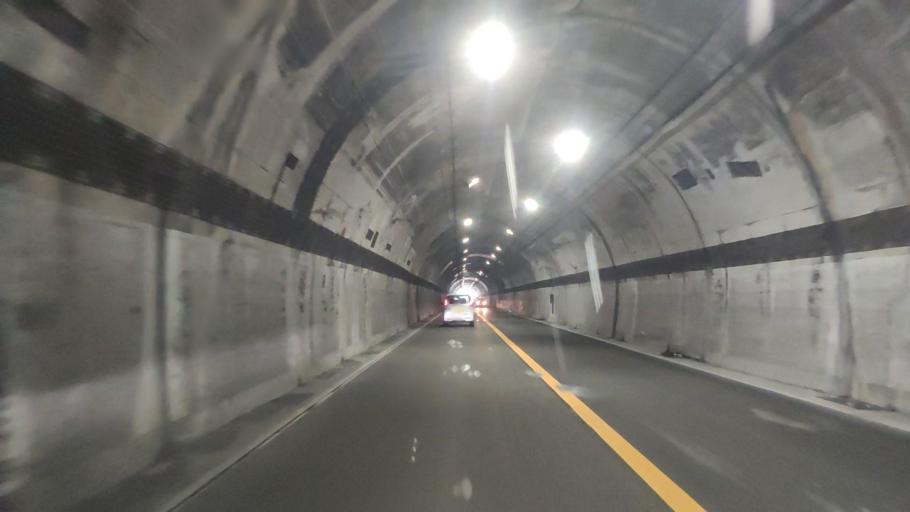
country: JP
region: Wakayama
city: Shingu
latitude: 33.5755
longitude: 135.9181
